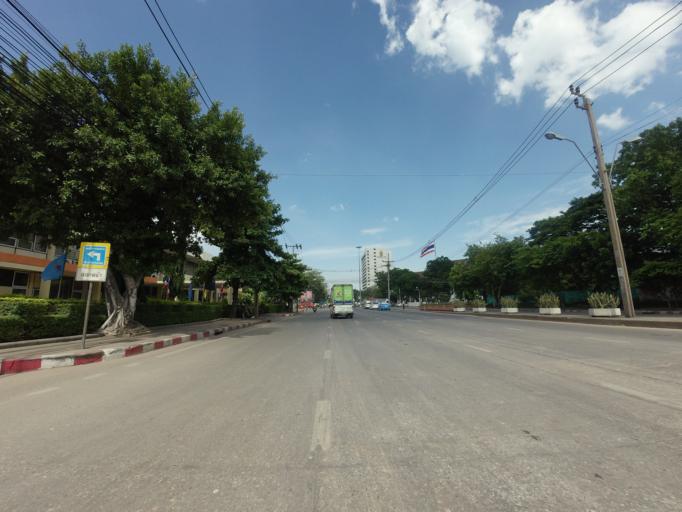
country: TH
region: Bangkok
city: Khlong Toei
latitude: 13.7151
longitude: 100.5644
